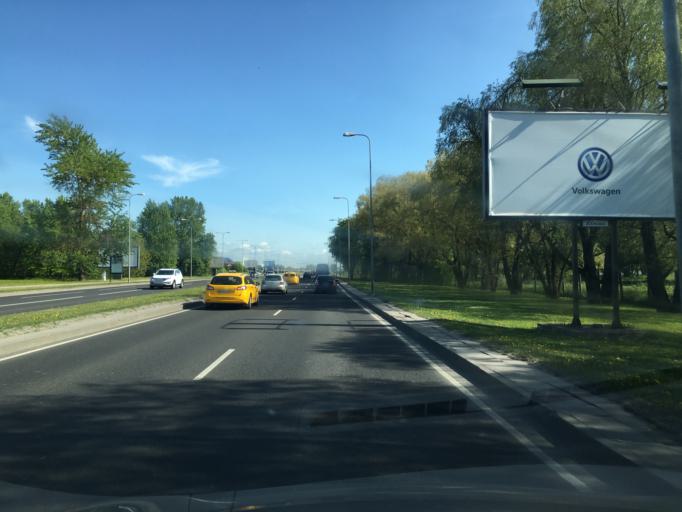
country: EE
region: Harju
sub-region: Tallinna linn
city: Tallinn
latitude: 59.4193
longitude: 24.7923
